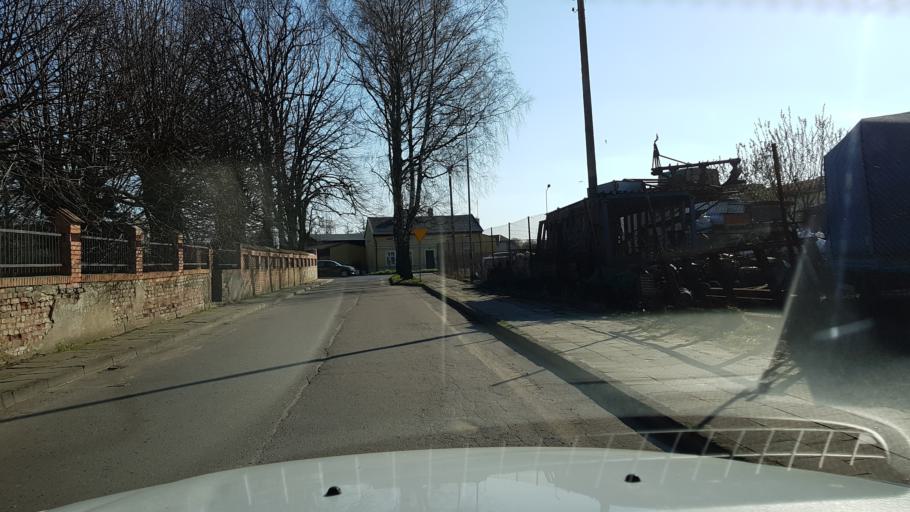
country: PL
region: West Pomeranian Voivodeship
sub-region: Powiat slawienski
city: Darlowo
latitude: 54.4147
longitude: 16.4150
